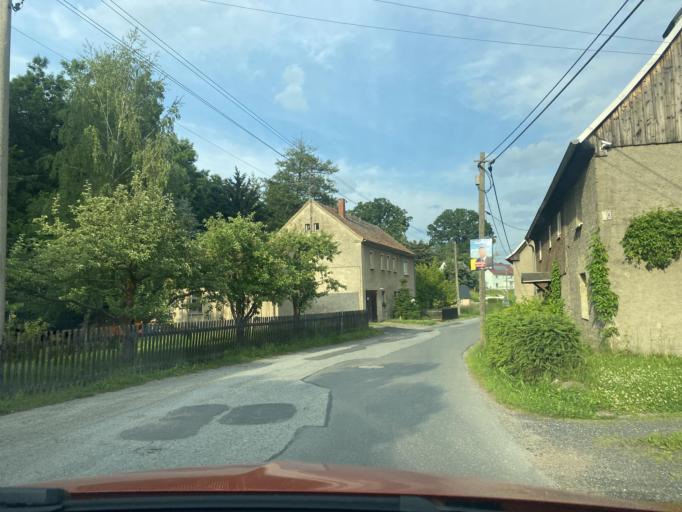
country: DE
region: Saxony
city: Grosshennersdorf
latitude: 51.0220
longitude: 14.7828
